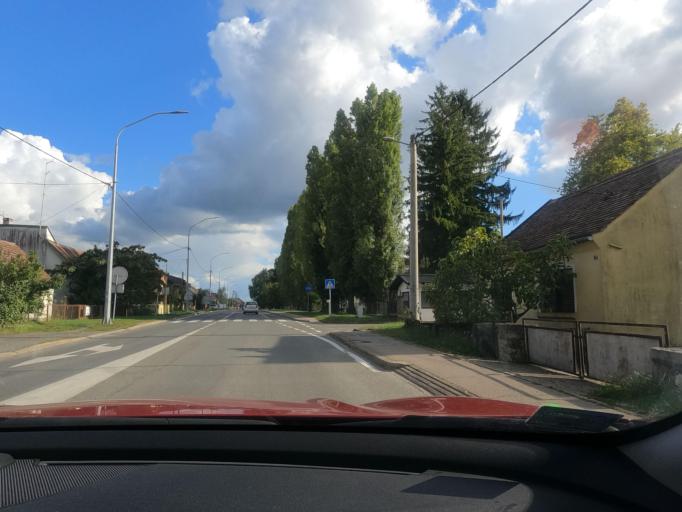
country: HR
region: Sisacko-Moslavacka
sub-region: Grad Sisak
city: Sisak
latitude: 45.4706
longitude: 16.3668
